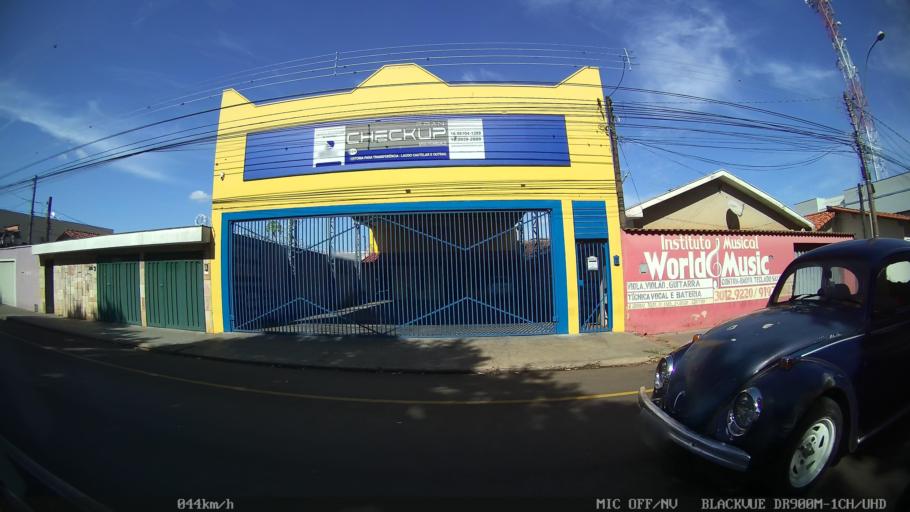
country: BR
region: Sao Paulo
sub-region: Franca
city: Franca
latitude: -20.5140
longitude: -47.4049
